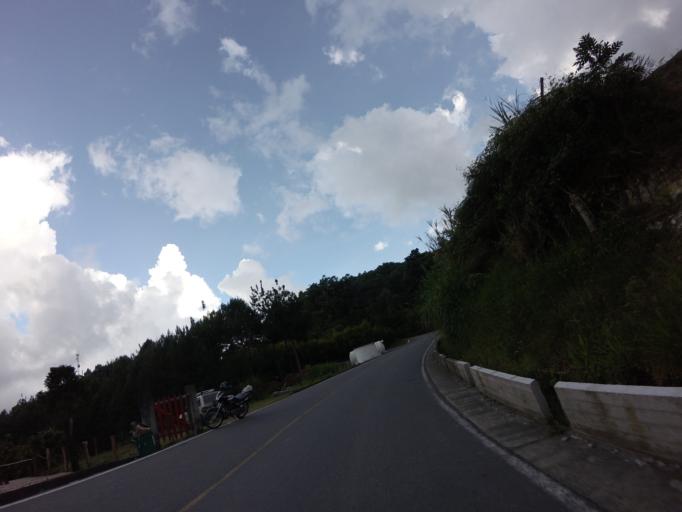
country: CO
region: Caldas
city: Pensilvania
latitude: 5.3787
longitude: -75.1511
